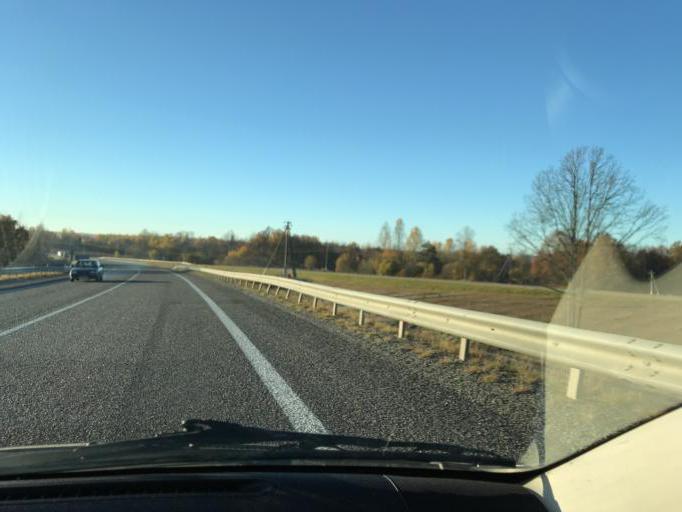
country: BY
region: Vitebsk
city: Vitebsk
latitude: 55.1011
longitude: 30.2998
